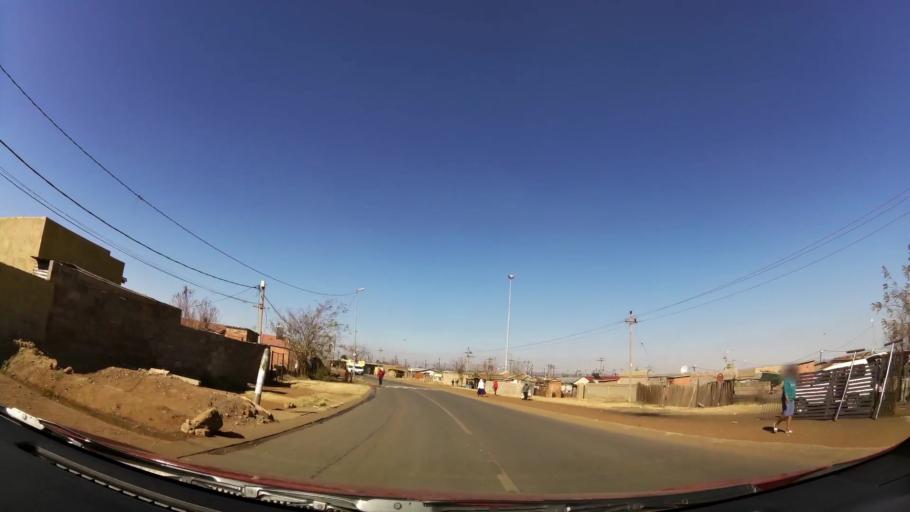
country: ZA
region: Gauteng
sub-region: City of Johannesburg Metropolitan Municipality
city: Soweto
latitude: -26.2233
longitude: 27.8195
